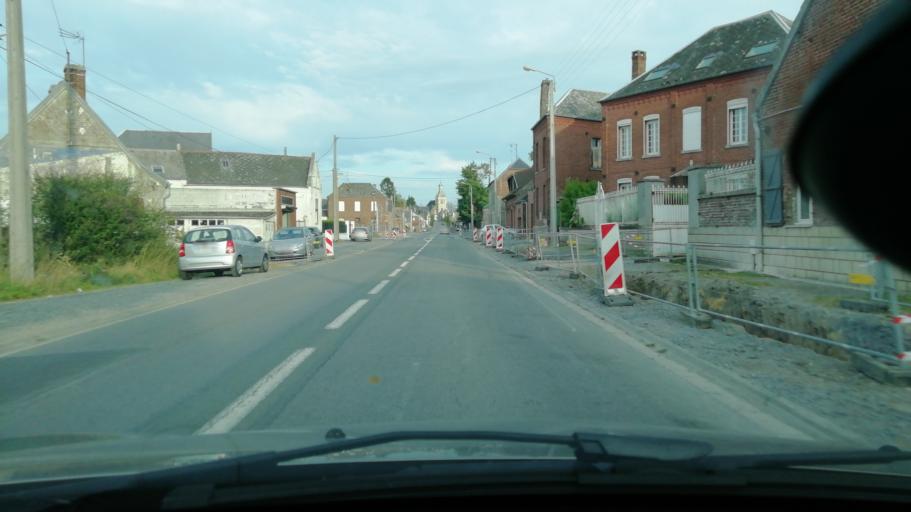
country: FR
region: Nord-Pas-de-Calais
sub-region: Departement du Nord
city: Viesly
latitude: 50.1243
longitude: 3.4539
